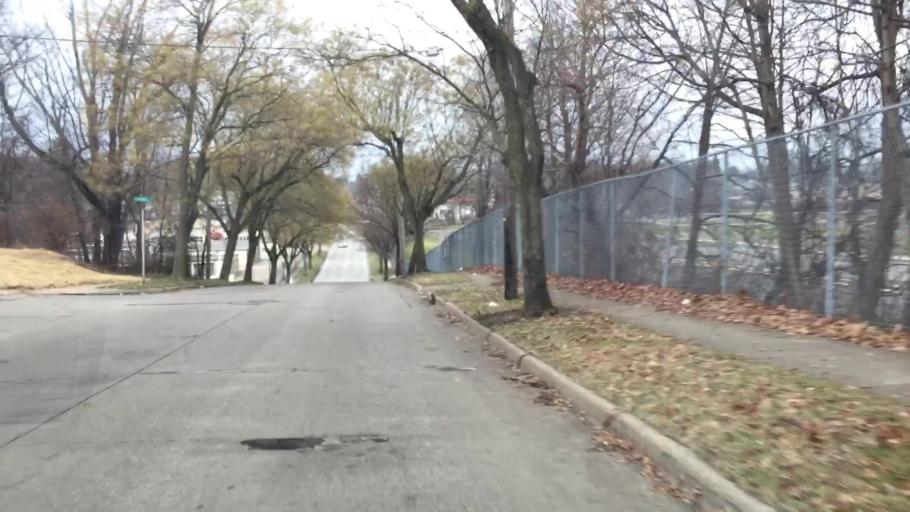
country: US
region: Ohio
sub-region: Summit County
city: Cuyahoga Falls
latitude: 41.1097
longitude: -81.5021
